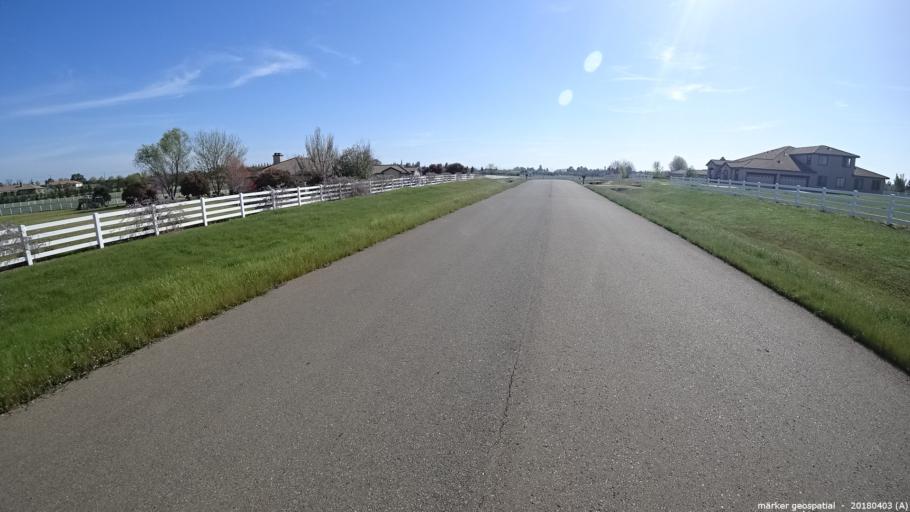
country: US
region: California
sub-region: Sacramento County
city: Wilton
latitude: 38.4185
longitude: -121.1935
